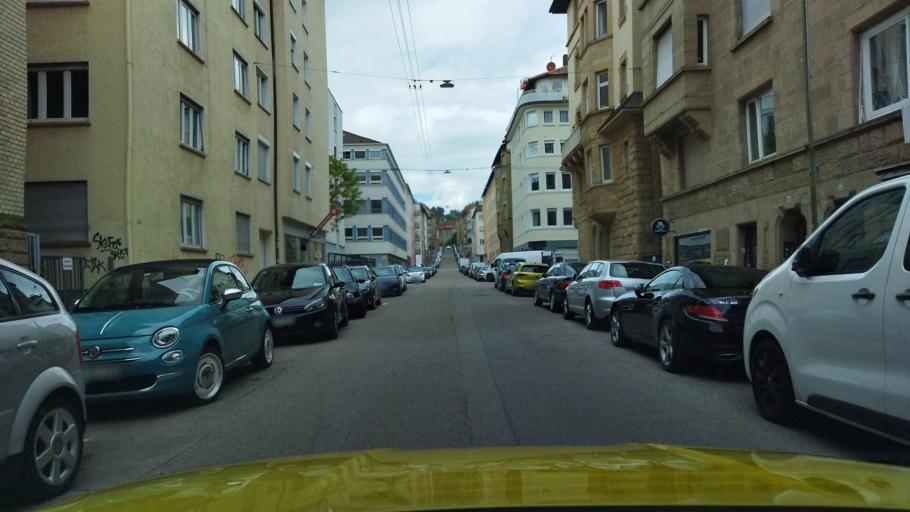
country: DE
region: Baden-Wuerttemberg
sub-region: Regierungsbezirk Stuttgart
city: Stuttgart
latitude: 48.7771
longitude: 9.1596
